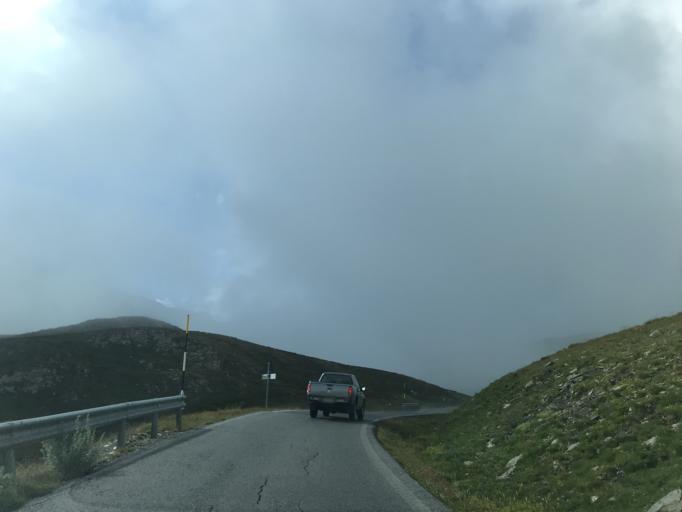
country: IT
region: Piedmont
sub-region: Provincia di Cuneo
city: Pontechianale
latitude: 44.6761
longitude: 6.9907
